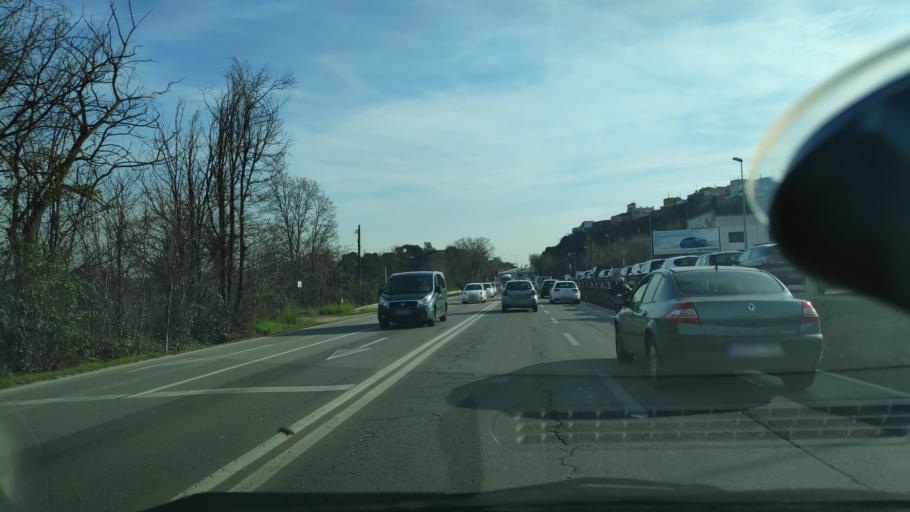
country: ES
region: Catalonia
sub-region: Provincia de Barcelona
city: Sabadell
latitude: 41.5704
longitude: 2.0969
